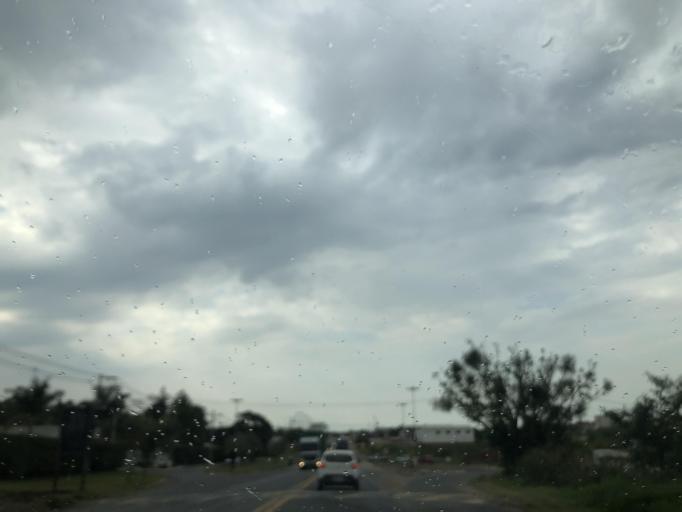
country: BR
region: Sao Paulo
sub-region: Salto De Pirapora
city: Salto de Pirapora
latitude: -23.6491
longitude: -47.5845
